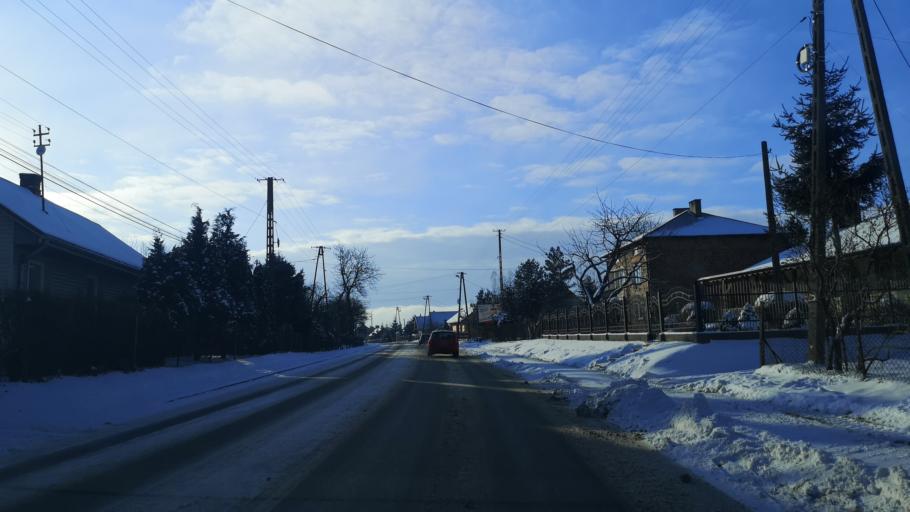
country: PL
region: Subcarpathian Voivodeship
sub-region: Powiat przeworski
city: Gorliczyna
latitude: 50.0926
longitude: 22.4913
